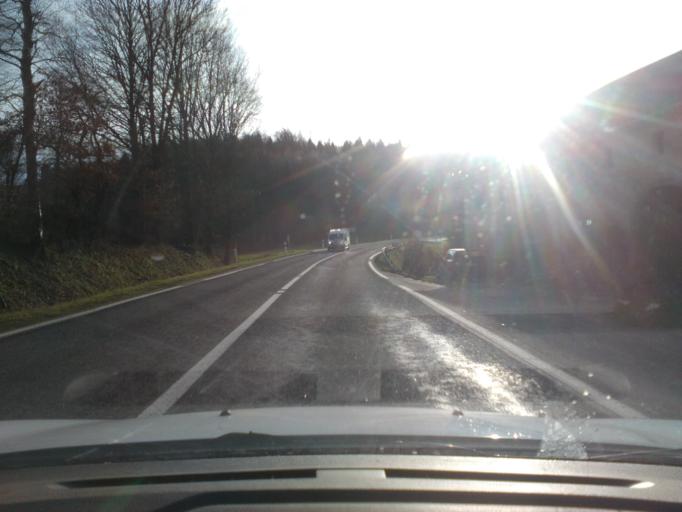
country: FR
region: Lorraine
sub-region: Departement des Vosges
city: Anould
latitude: 48.1806
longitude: 6.9372
